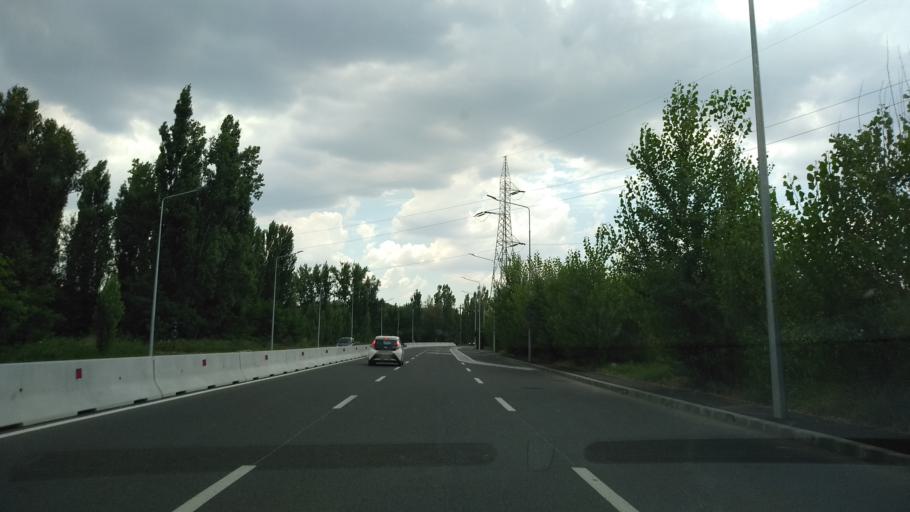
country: RO
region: Ilfov
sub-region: Comuna Popesti-Leordeni
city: Popesti-Leordeni
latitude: 44.3941
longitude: 26.1569
